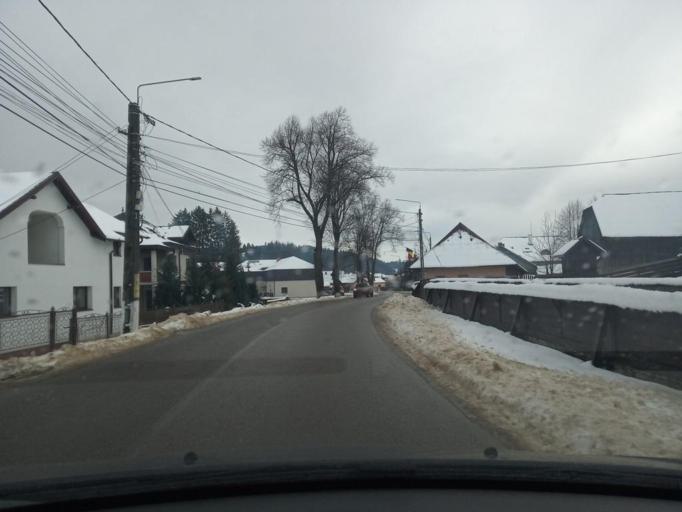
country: RO
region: Suceava
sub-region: Comuna Manastirea Humorului
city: Manastirea Humorului
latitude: 47.5928
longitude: 25.8609
